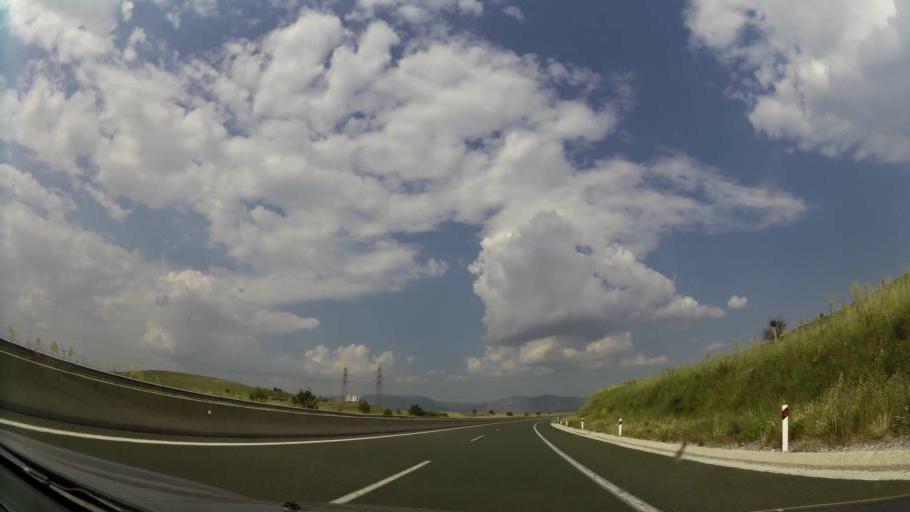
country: GR
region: West Macedonia
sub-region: Nomos Kozanis
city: Koila
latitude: 40.3605
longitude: 21.8178
